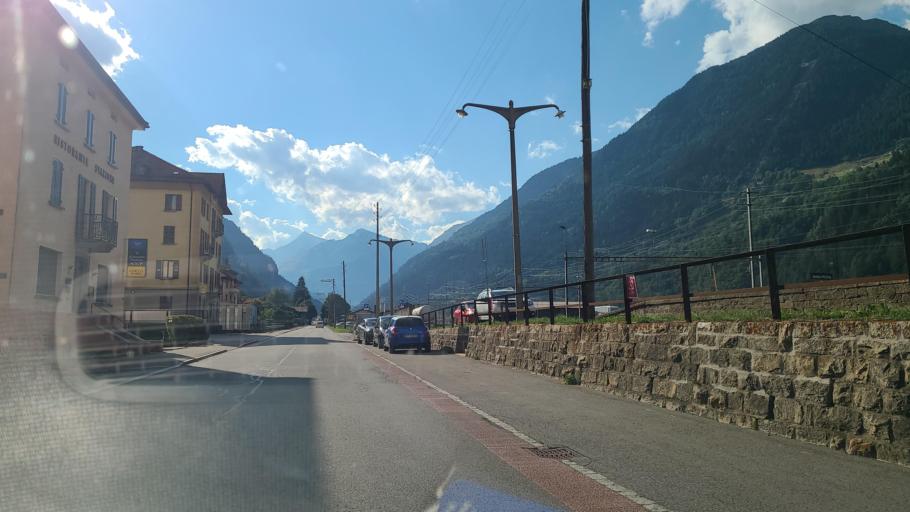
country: CH
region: Ticino
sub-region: Leventina District
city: Airolo
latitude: 46.5106
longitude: 8.6898
